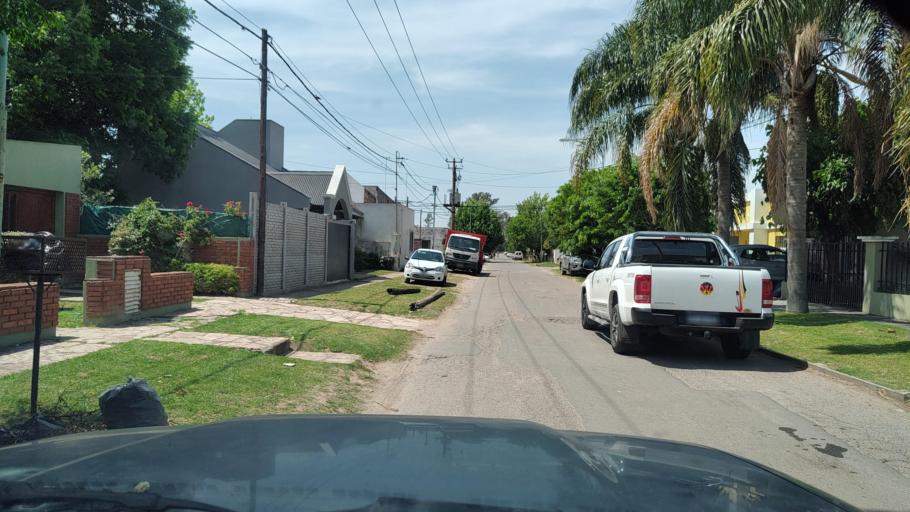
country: AR
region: Buenos Aires
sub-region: Partido de Lujan
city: Lujan
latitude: -34.6026
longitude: -59.1737
